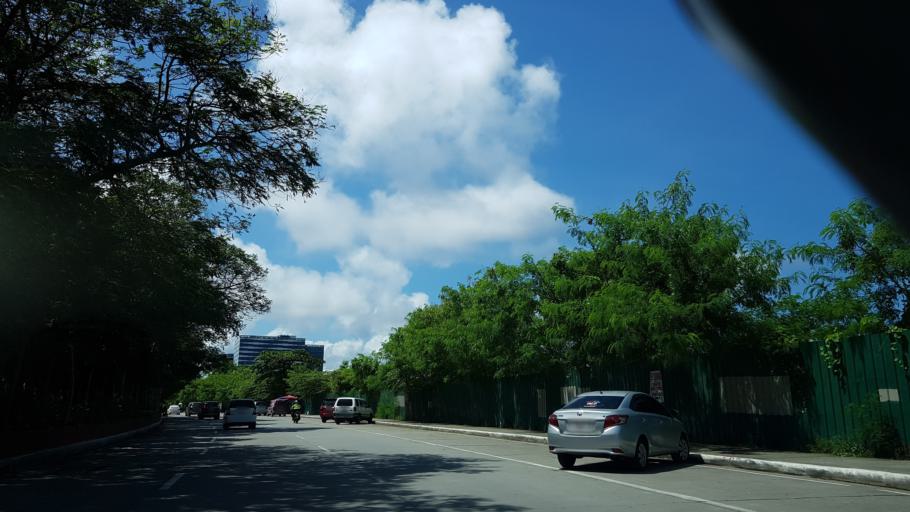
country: PH
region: Metro Manila
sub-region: City of Manila
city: Port Area
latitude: 14.5475
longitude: 120.9818
